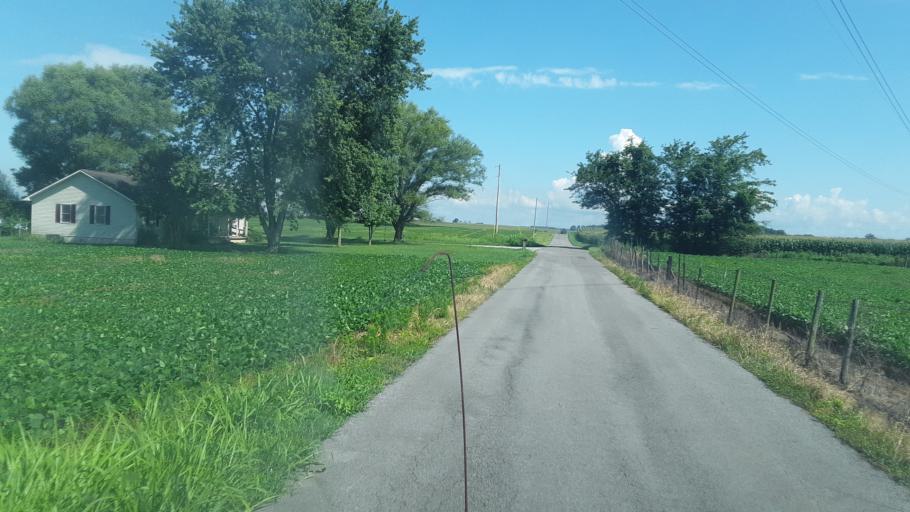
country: US
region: Kentucky
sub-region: Todd County
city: Elkton
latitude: 36.7579
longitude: -87.2272
